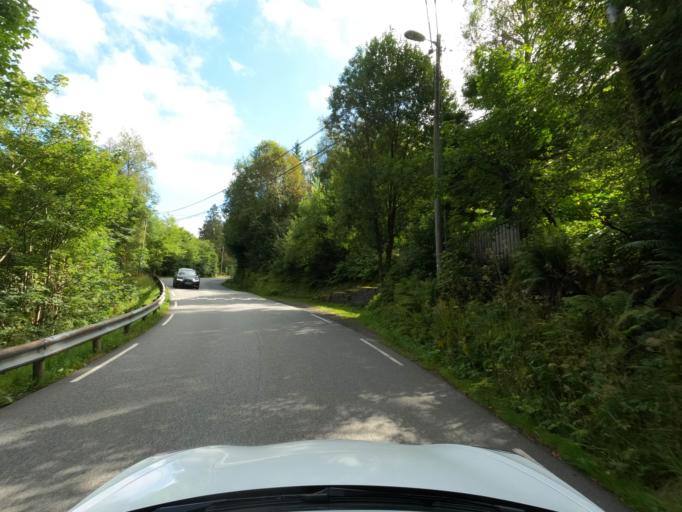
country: NO
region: Hordaland
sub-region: Os
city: Syfteland
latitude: 60.2731
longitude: 5.3717
